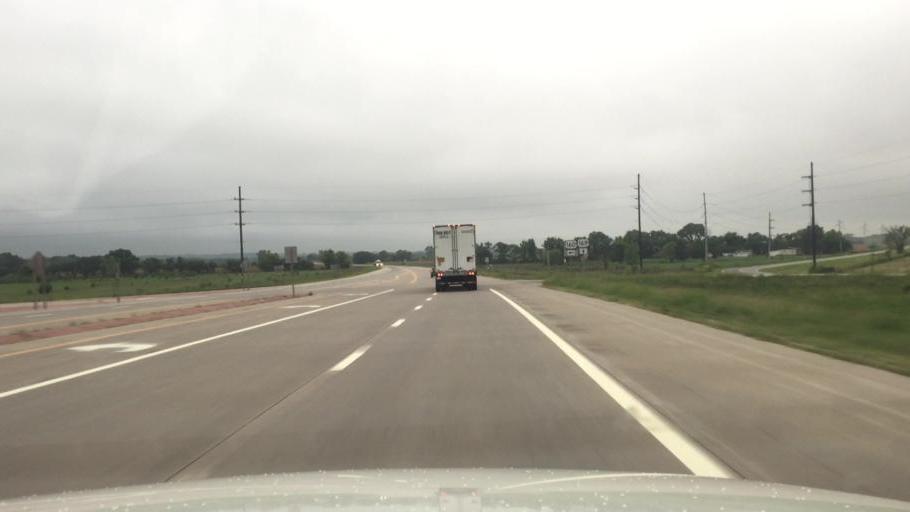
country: US
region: Kansas
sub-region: Montgomery County
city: Cherryvale
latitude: 37.2098
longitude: -95.5851
